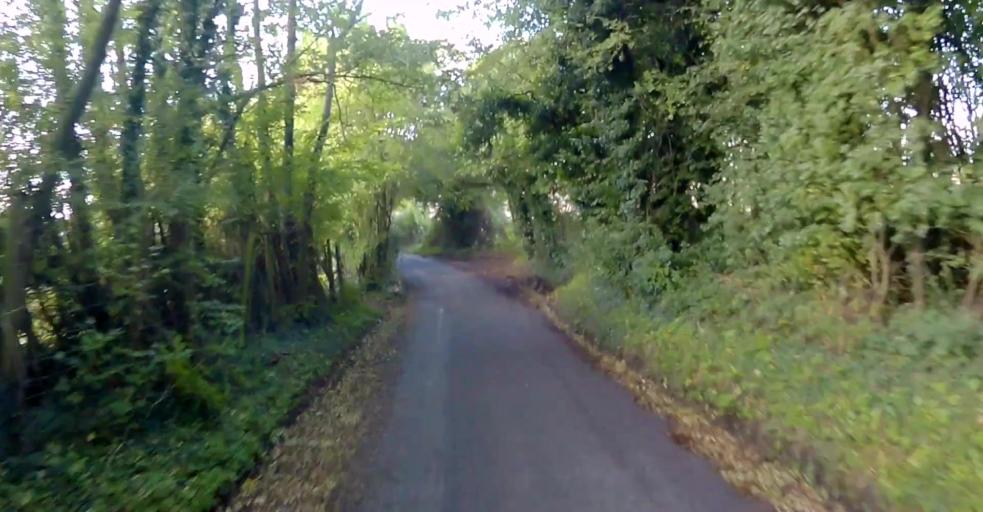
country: GB
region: England
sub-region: Hampshire
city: Long Sutton
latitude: 51.2098
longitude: -0.9039
